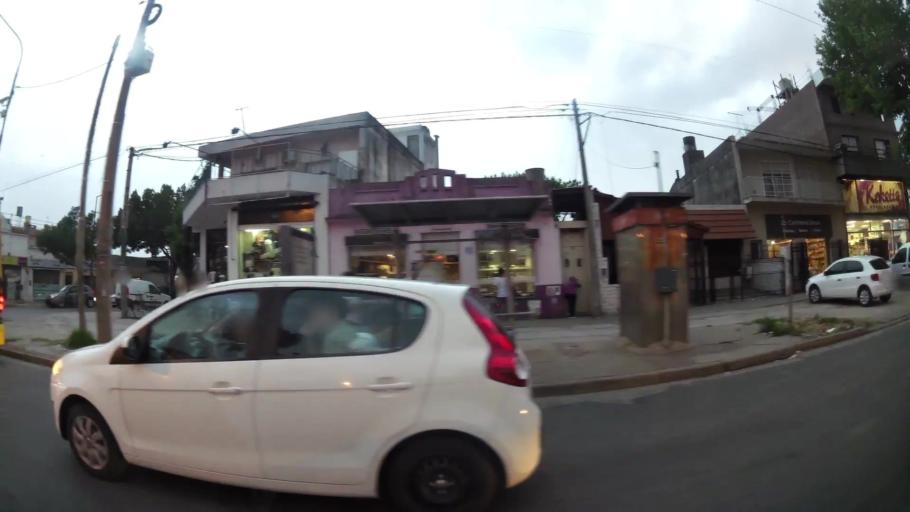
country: AR
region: Santa Fe
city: Granadero Baigorria
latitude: -32.8842
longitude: -60.6957
